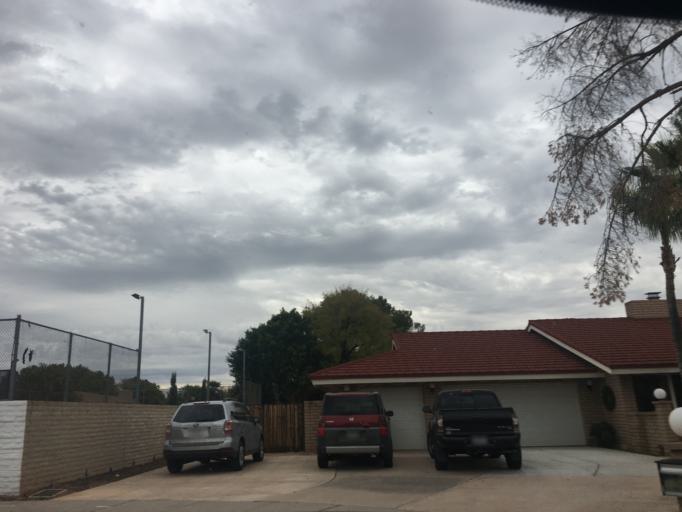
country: US
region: Arizona
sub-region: Maricopa County
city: Guadalupe
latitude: 33.3650
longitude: -111.9265
